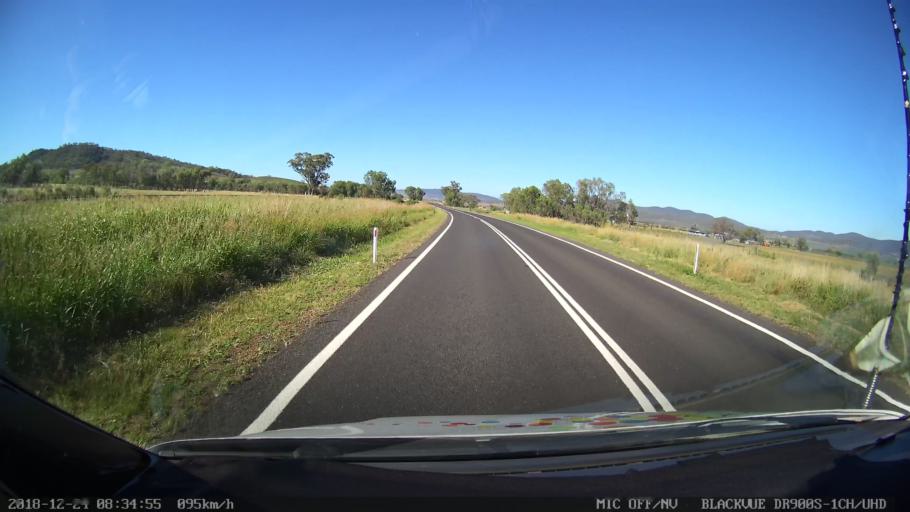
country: AU
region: New South Wales
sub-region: Liverpool Plains
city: Quirindi
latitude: -31.2964
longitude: 150.6643
